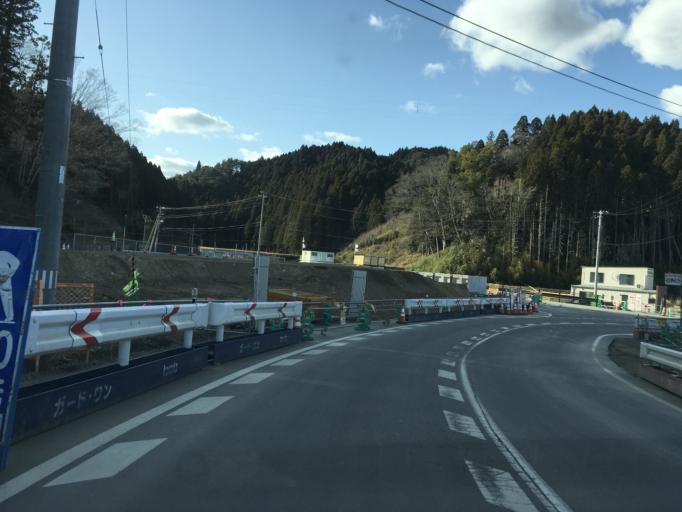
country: JP
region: Iwate
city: Ofunato
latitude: 39.0158
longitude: 141.6136
